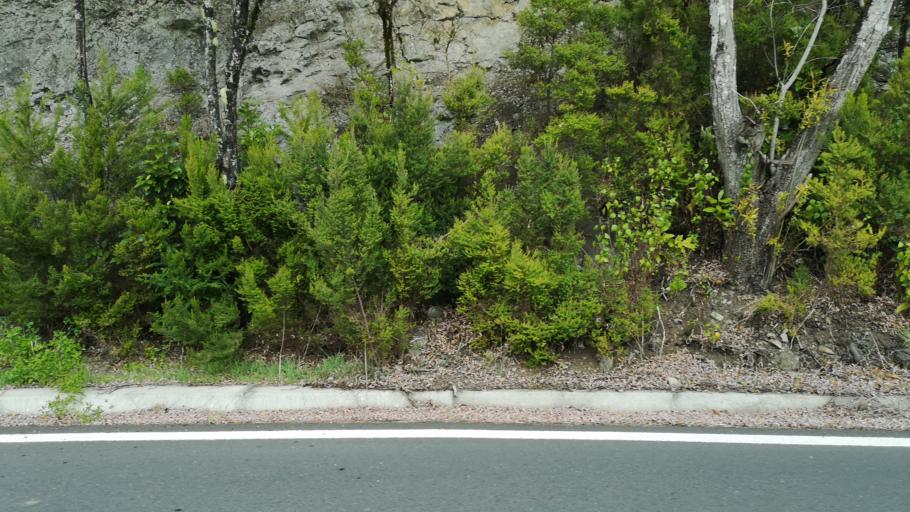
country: ES
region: Canary Islands
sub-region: Provincia de Santa Cruz de Tenerife
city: Alajero
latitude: 28.1095
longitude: -17.2427
